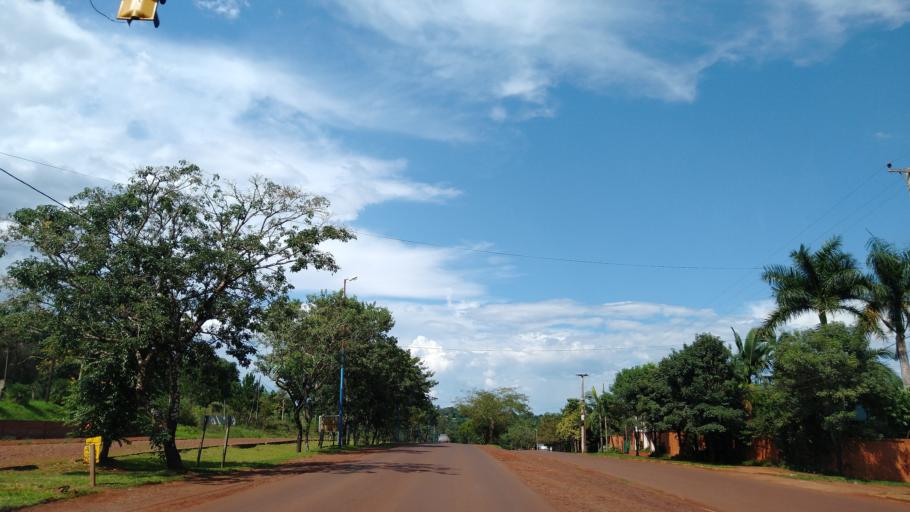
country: AR
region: Misiones
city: Puerto Libertad
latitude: -25.9704
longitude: -54.5716
